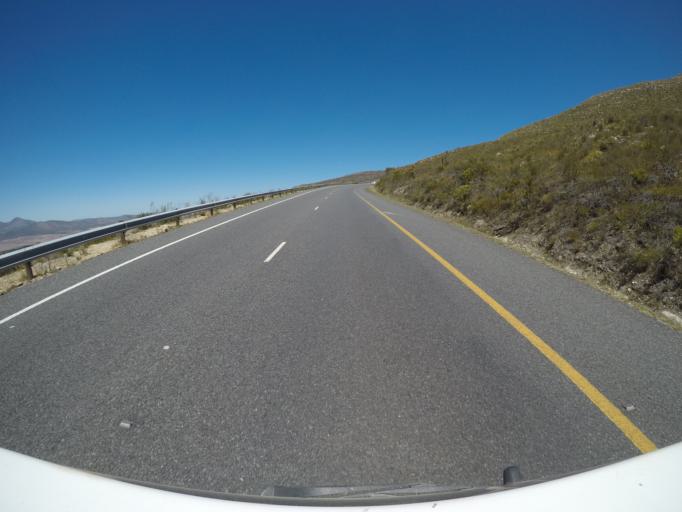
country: ZA
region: Western Cape
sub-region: Overberg District Municipality
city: Grabouw
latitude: -34.2208
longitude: 19.1837
